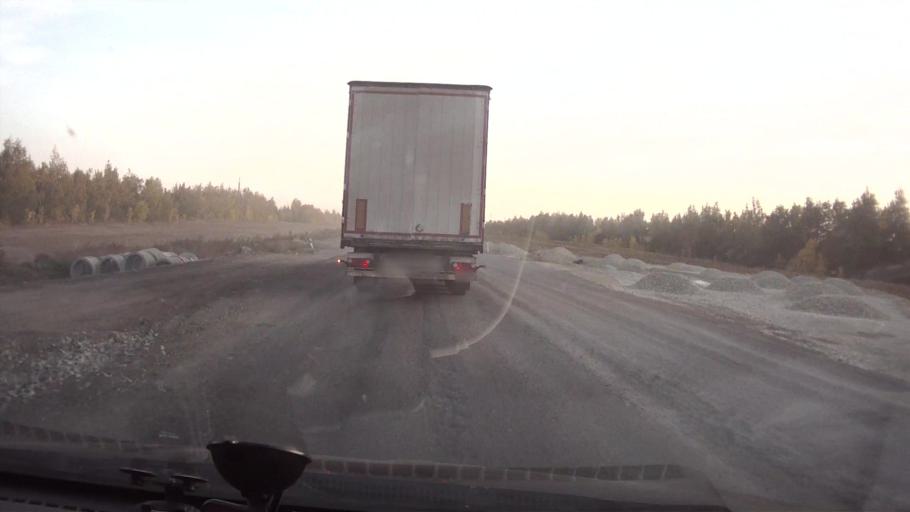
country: RU
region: Saratov
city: Kamenskiy
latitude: 50.9265
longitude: 45.5992
